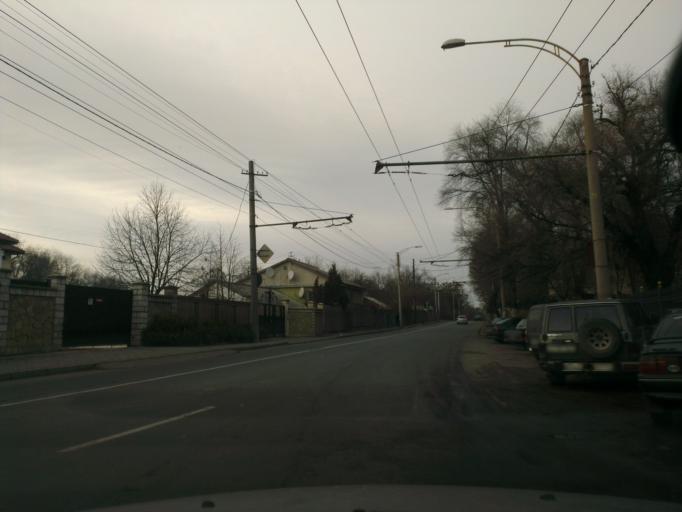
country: MD
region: Chisinau
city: Chisinau
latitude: 47.0289
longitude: 28.8172
